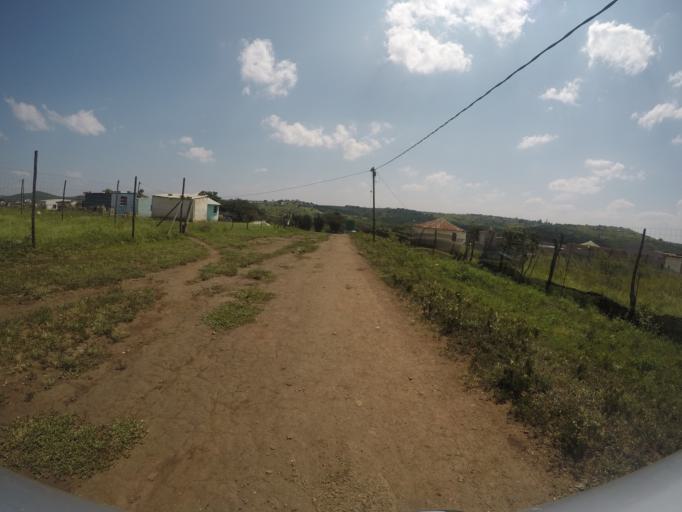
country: ZA
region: KwaZulu-Natal
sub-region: uThungulu District Municipality
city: Empangeni
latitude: -28.5913
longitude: 31.7374
